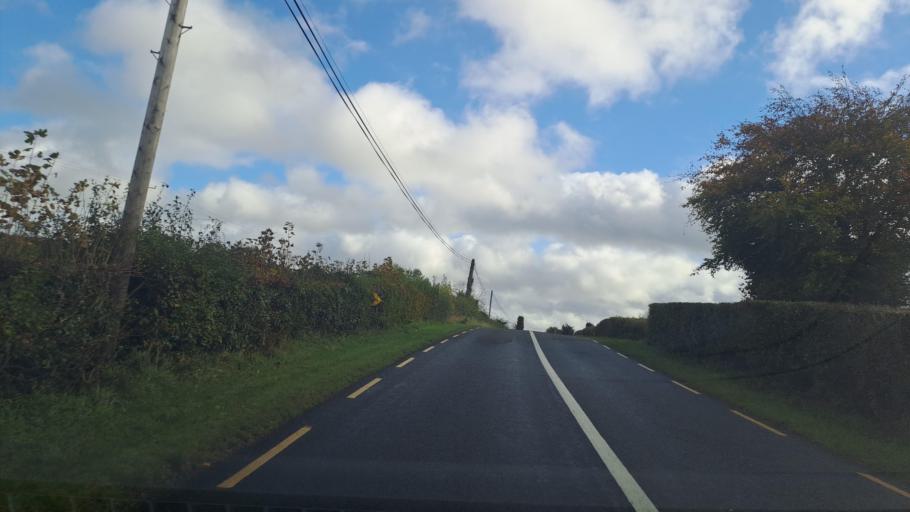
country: IE
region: Ulster
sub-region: County Monaghan
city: Monaghan
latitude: 54.1308
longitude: -6.9275
